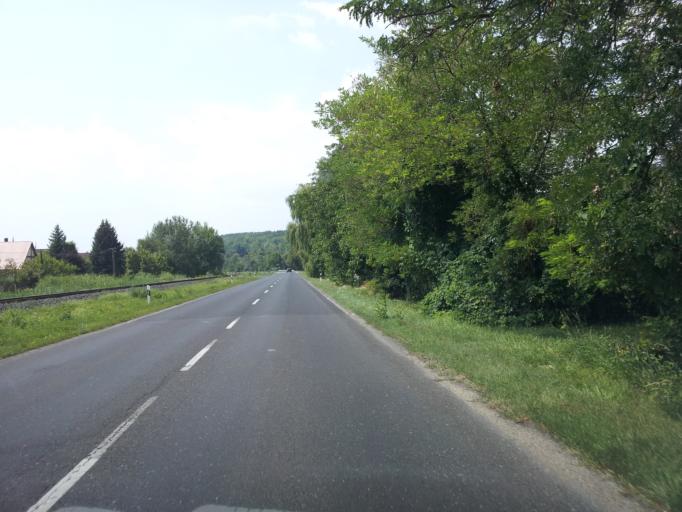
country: HU
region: Veszprem
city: Balatonkenese
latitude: 47.0368
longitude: 18.0867
